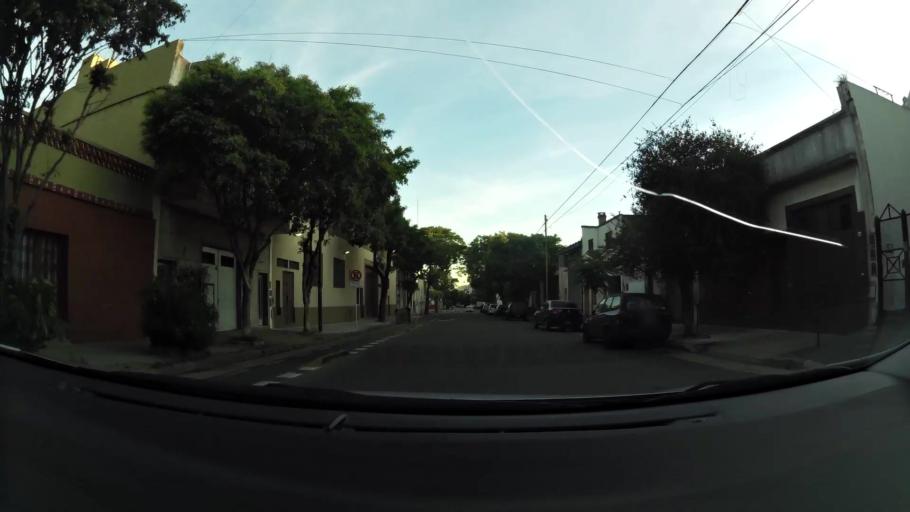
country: AR
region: Buenos Aires F.D.
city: Buenos Aires
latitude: -34.6349
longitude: -58.4211
